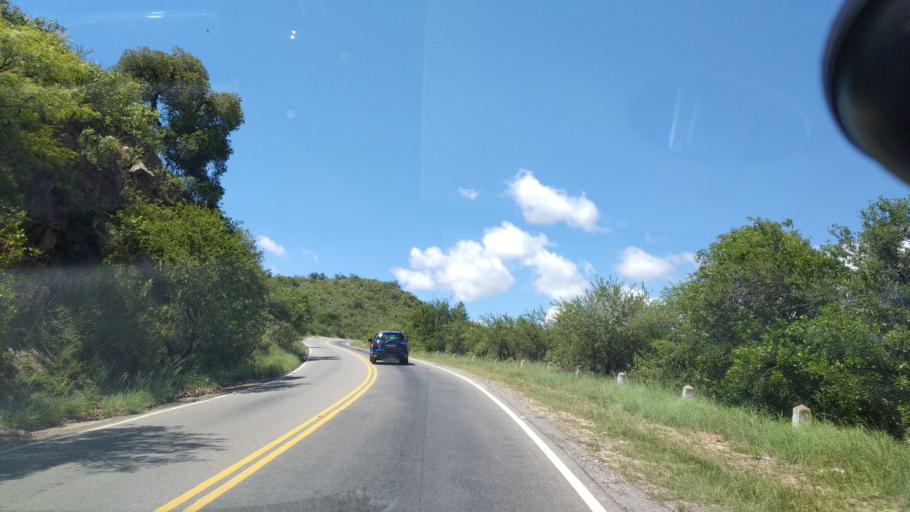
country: AR
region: Cordoba
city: Villa Cura Brochero
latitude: -31.6943
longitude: -65.0516
